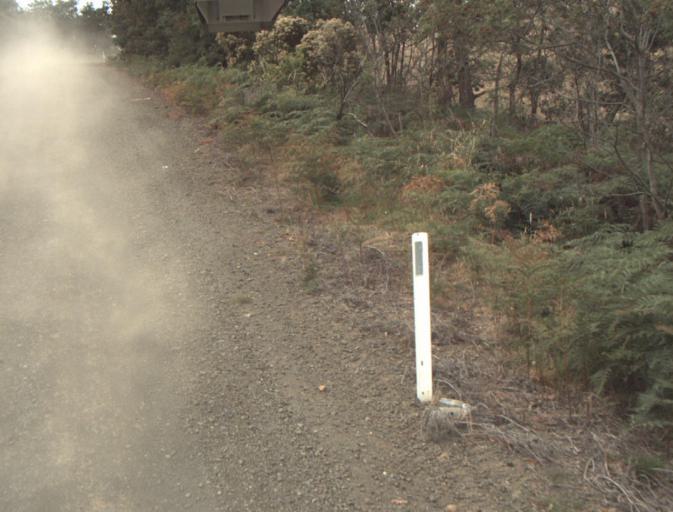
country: AU
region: Tasmania
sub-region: Northern Midlands
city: Evandale
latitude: -41.5183
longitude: 147.4154
